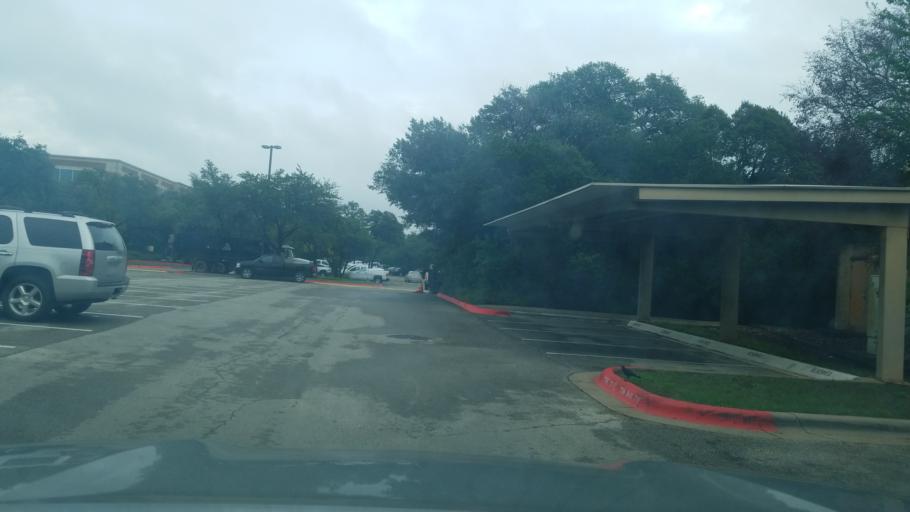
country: US
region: Texas
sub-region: Travis County
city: Rollingwood
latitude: 30.2418
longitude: -97.7994
